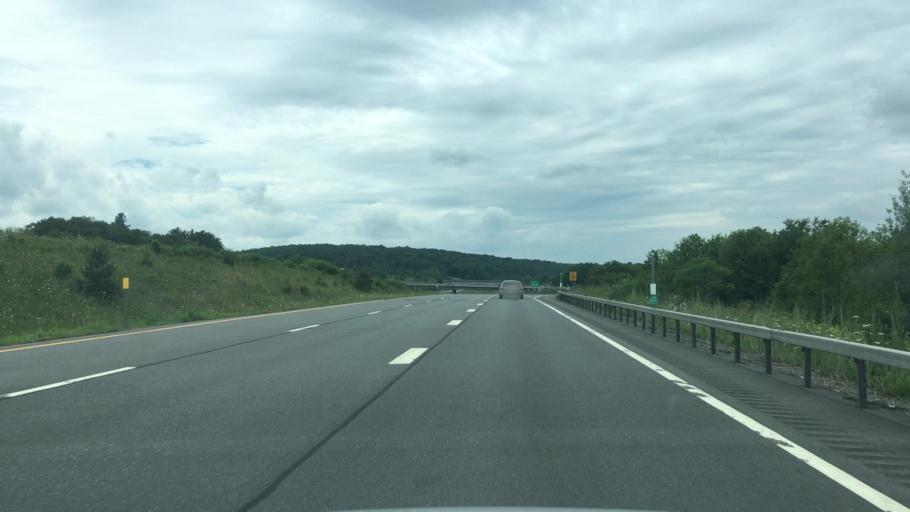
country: US
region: New York
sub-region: Albany County
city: Altamont
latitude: 42.7647
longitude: -74.1094
